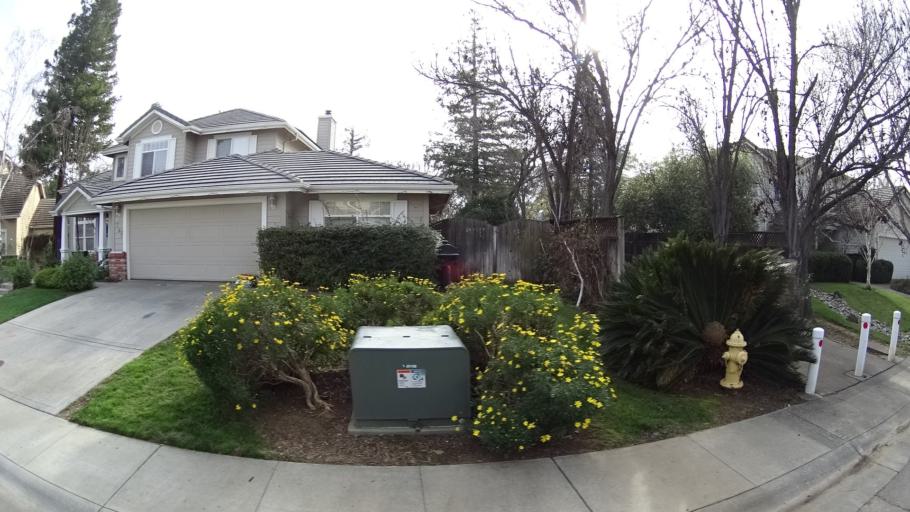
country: US
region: California
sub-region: Yolo County
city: Davis
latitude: 38.5356
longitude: -121.7222
